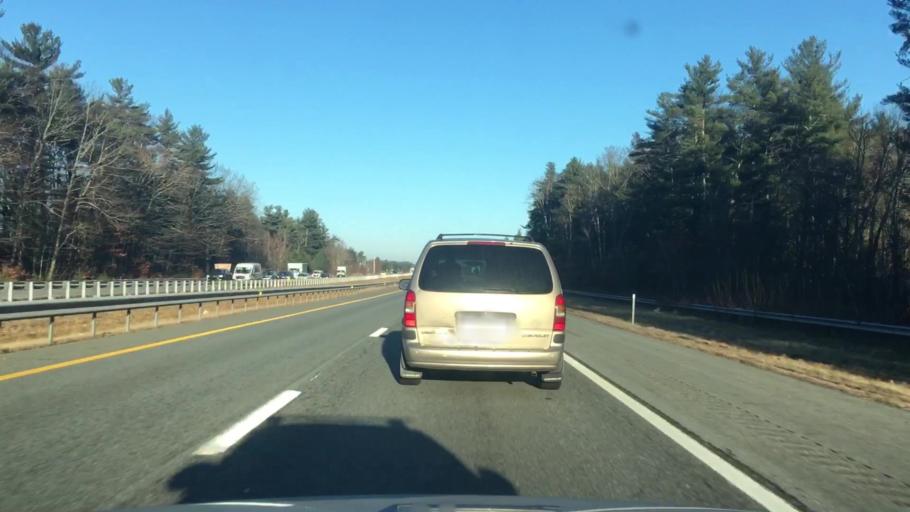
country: US
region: New Hampshire
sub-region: Rockingham County
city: Exeter
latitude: 42.9840
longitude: -70.9176
